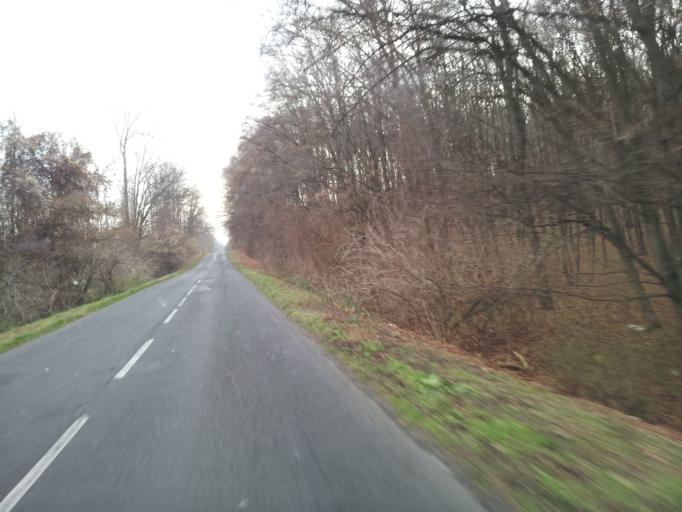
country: HU
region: Veszprem
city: Sumeg
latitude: 46.9030
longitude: 17.2376
